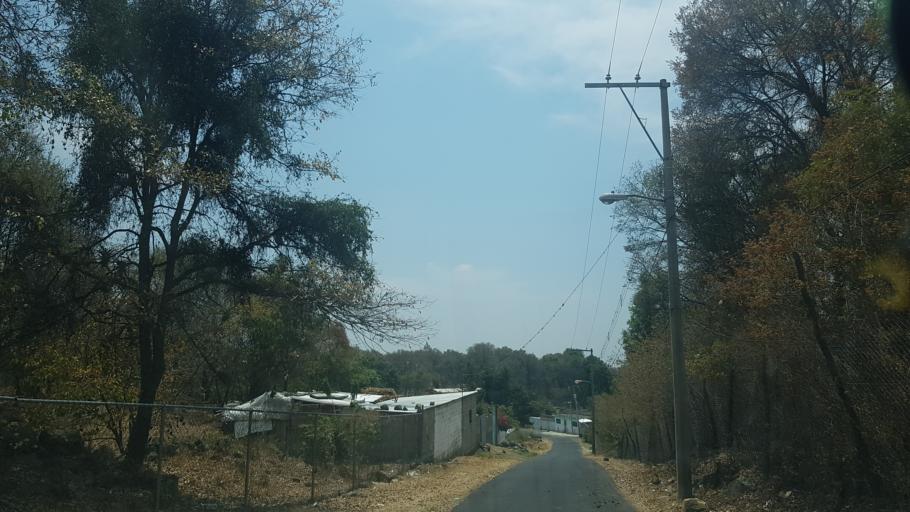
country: MX
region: Puebla
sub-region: Tochimilco
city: La Magdalena Yancuitlalpan
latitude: 18.8883
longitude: -98.6026
